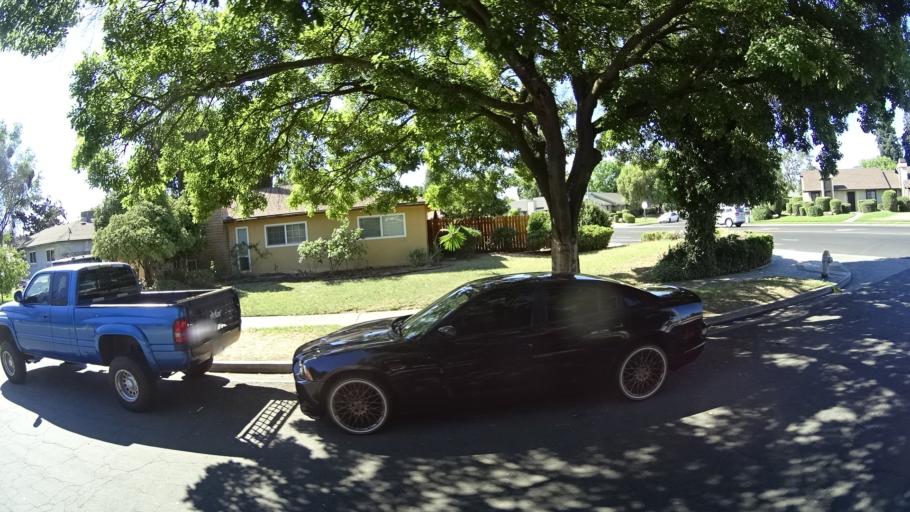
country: US
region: California
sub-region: Fresno County
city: West Park
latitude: 36.8056
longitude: -119.8529
